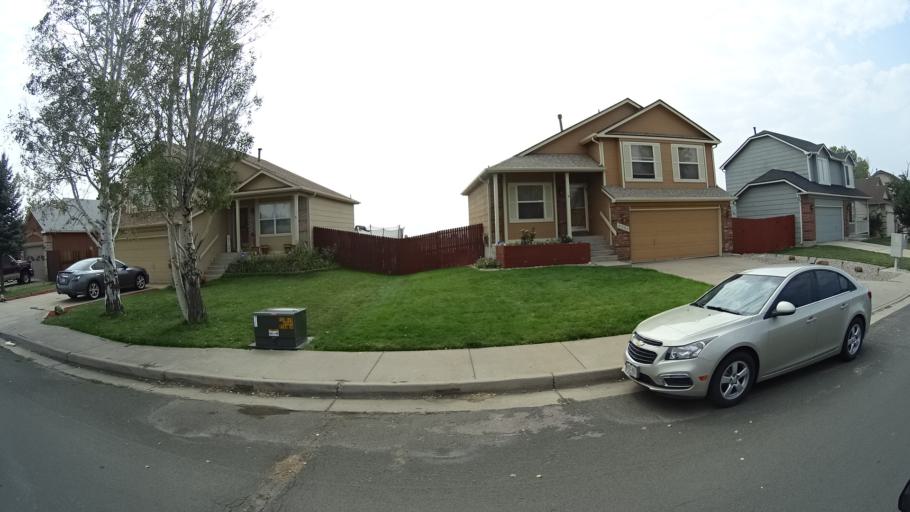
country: US
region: Colorado
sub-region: El Paso County
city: Stratmoor
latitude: 38.8205
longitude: -104.7480
